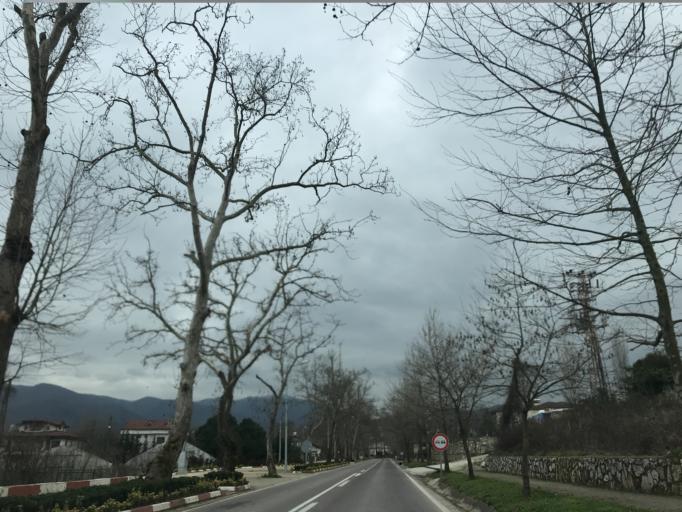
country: TR
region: Yalova
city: Kadikoy
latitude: 40.6140
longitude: 29.2141
